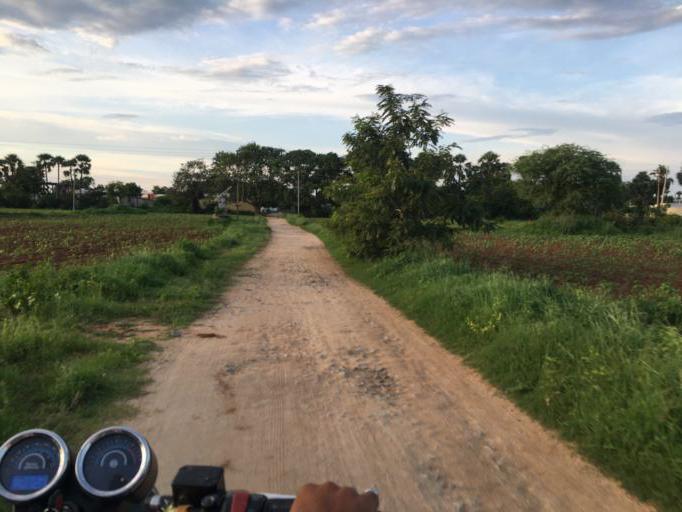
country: IN
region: Telangana
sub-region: Nalgonda
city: Nalgonda
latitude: 17.1719
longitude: 79.4174
